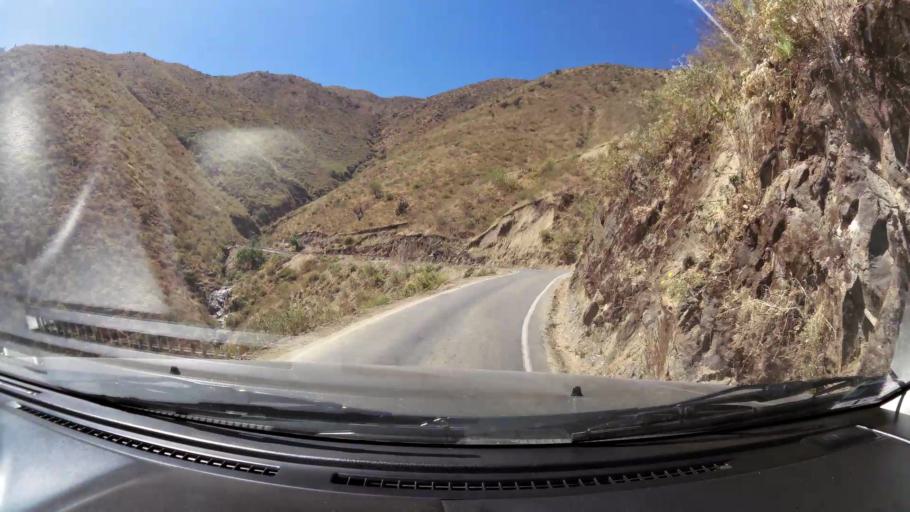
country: PE
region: Ica
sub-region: Provincia de Pisco
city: Huancano
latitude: -13.7209
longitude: -75.4517
